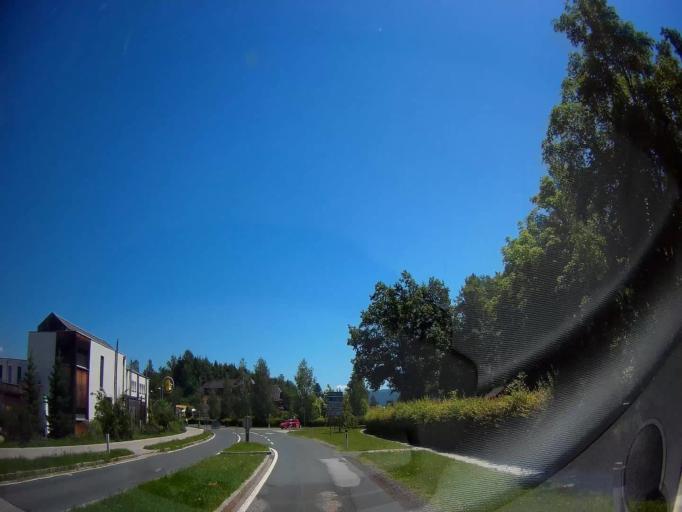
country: AT
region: Carinthia
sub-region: Politischer Bezirk Klagenfurt Land
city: Kottmannsdorf
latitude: 46.6064
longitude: 14.2538
